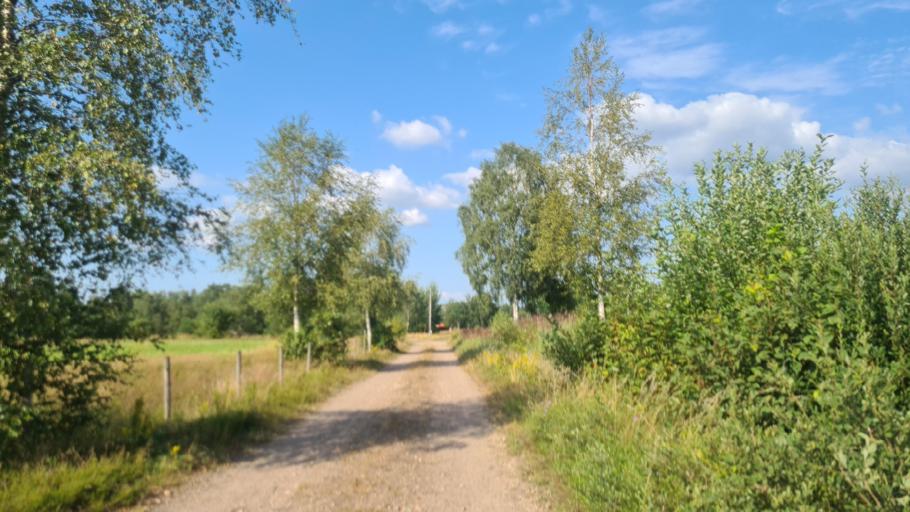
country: SE
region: Kronoberg
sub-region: Ljungby Kommun
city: Ljungby
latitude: 56.7757
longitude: 13.9019
